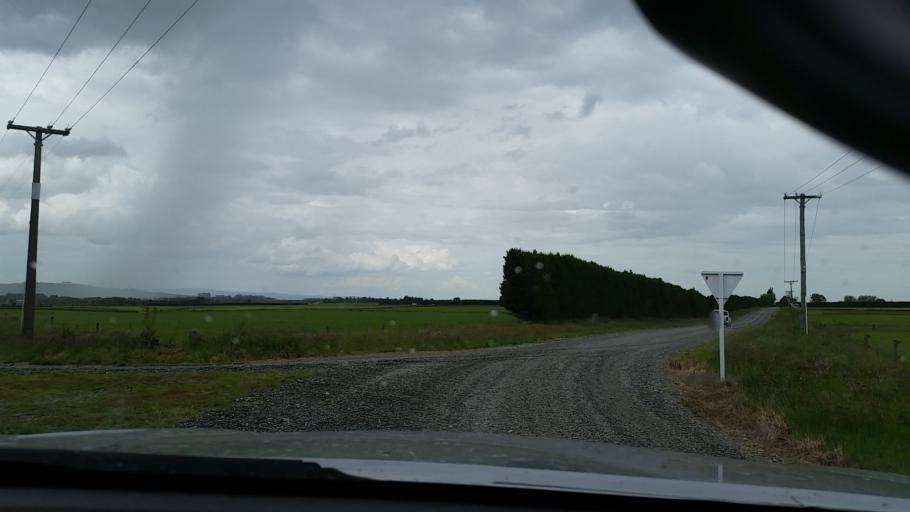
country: NZ
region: Southland
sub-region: Southland District
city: Winton
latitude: -46.0069
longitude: 168.2168
